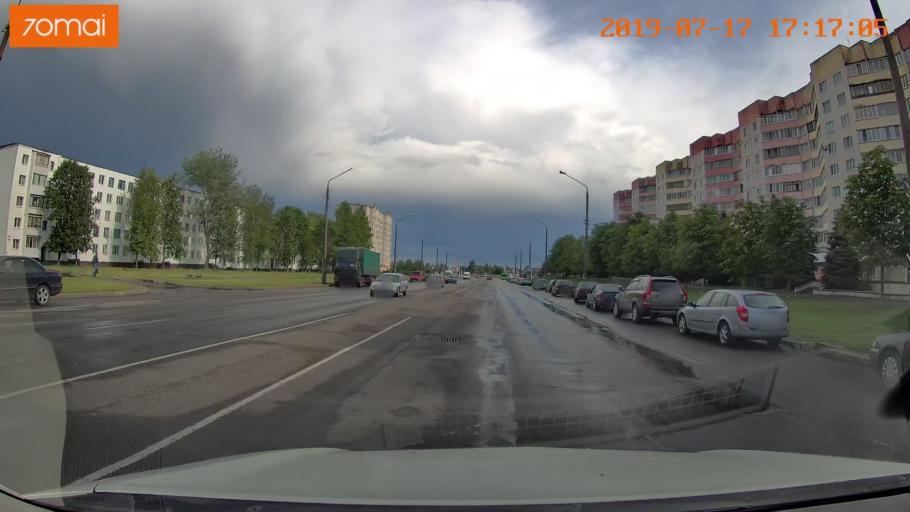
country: BY
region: Mogilev
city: Babruysk
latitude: 53.1633
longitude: 29.1971
